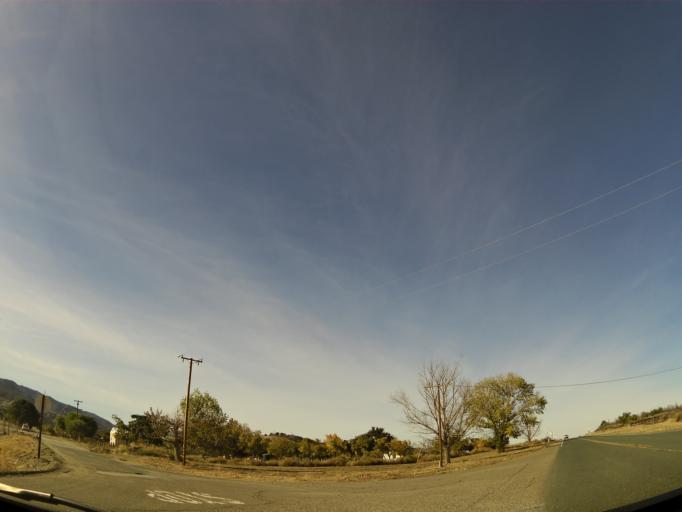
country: US
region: California
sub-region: San Benito County
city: Ridgemark
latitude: 36.6663
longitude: -121.2484
